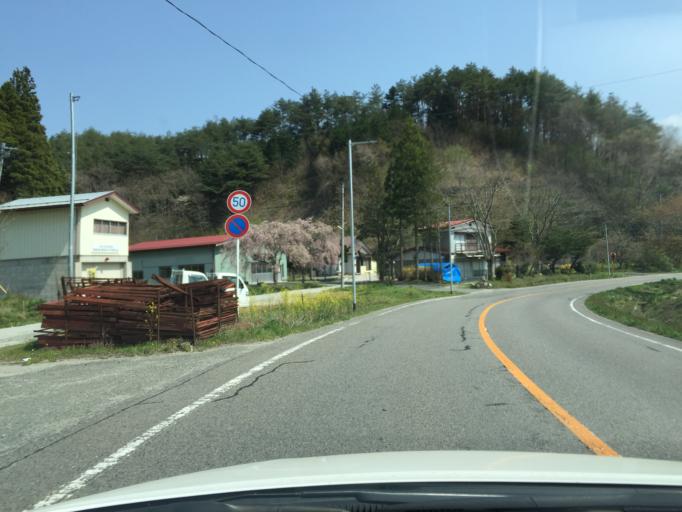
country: JP
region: Fukushima
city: Funehikimachi-funehiki
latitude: 37.4567
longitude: 140.7627
